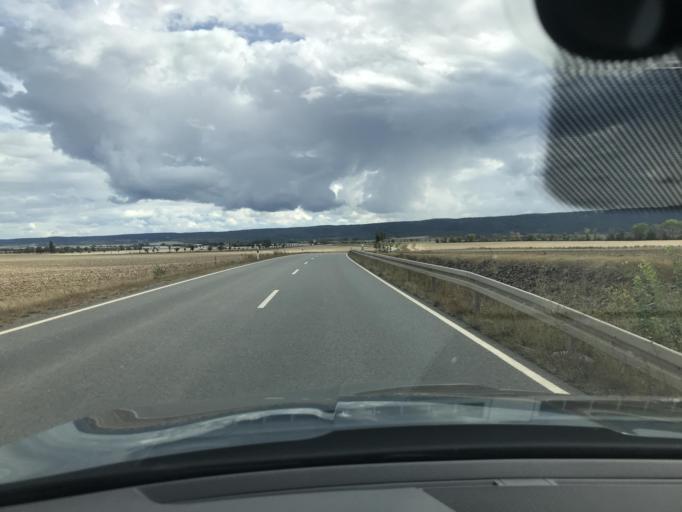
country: DE
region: Saxony-Anhalt
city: Westerhausen
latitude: 51.7883
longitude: 11.0473
